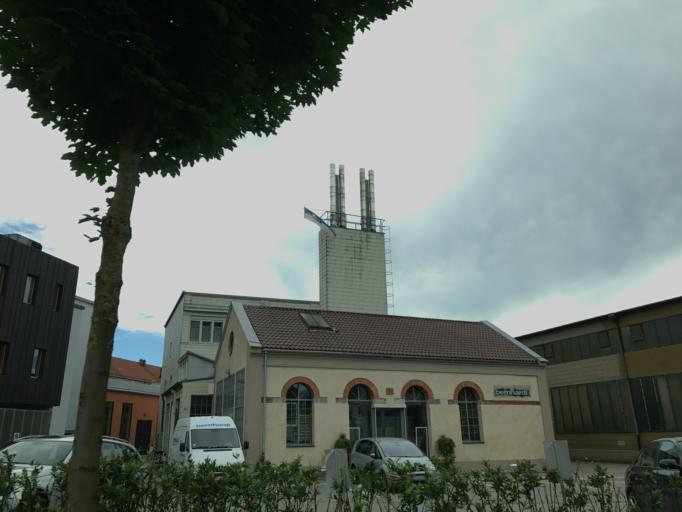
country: DE
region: Baden-Wuerttemberg
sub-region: Tuebingen Region
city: Ravensburg
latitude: 47.7860
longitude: 9.6100
